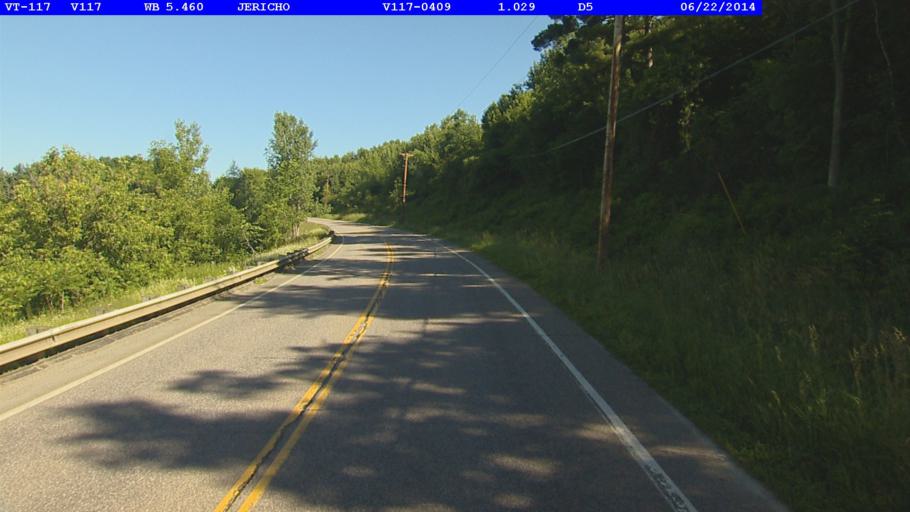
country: US
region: Vermont
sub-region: Chittenden County
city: Jericho
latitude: 44.4597
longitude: -73.0202
